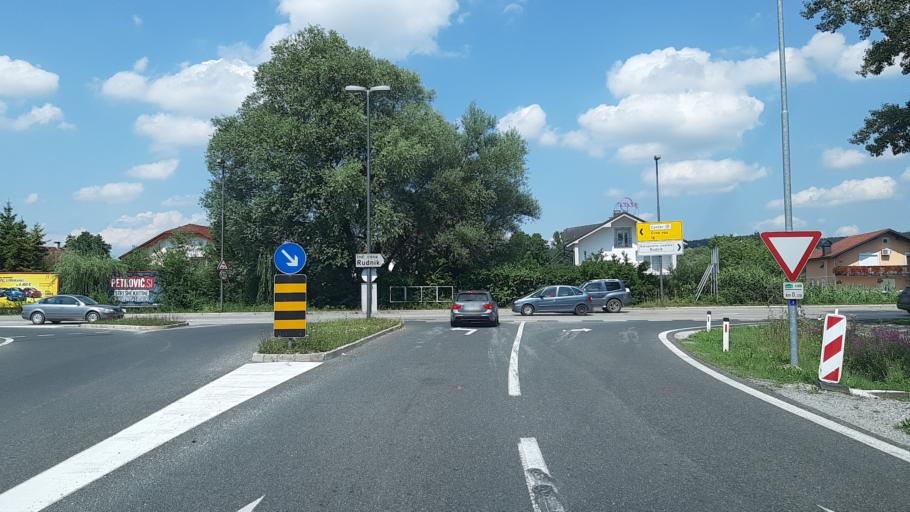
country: SI
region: Skofljica
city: Lavrica
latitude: 46.0182
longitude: 14.5250
